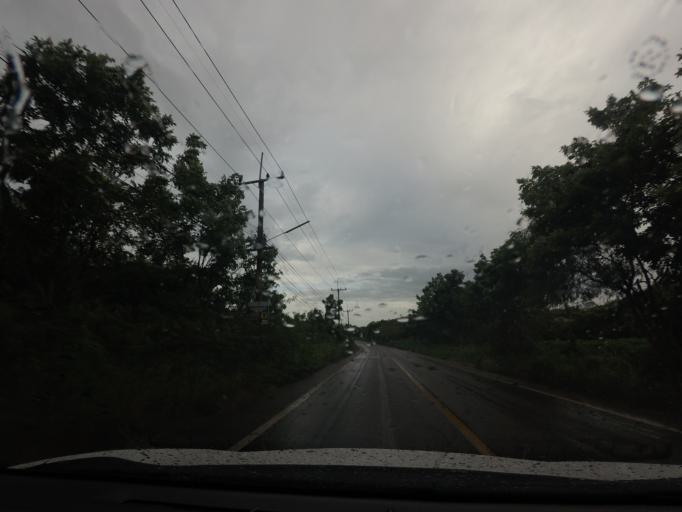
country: TH
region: Chon Buri
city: Sattahip
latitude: 12.6825
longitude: 100.9508
